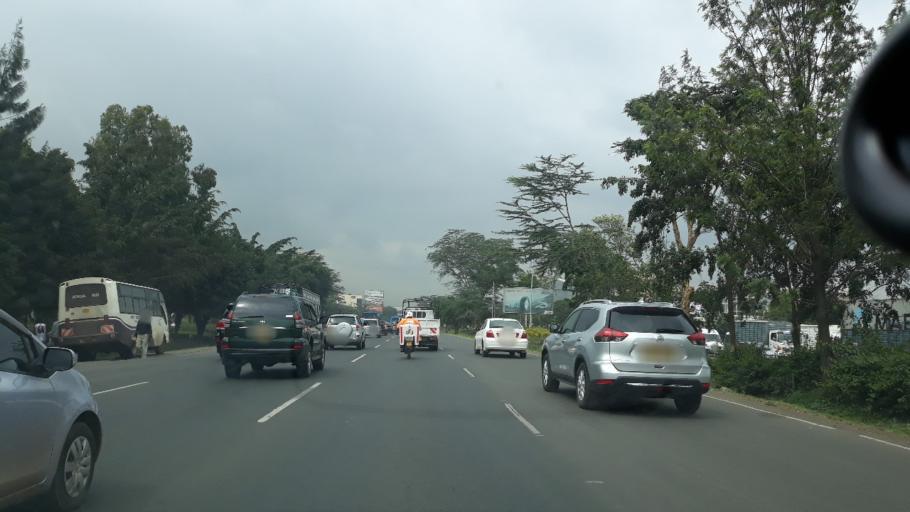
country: KE
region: Nairobi Area
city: Pumwani
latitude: -1.3302
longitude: 36.8702
